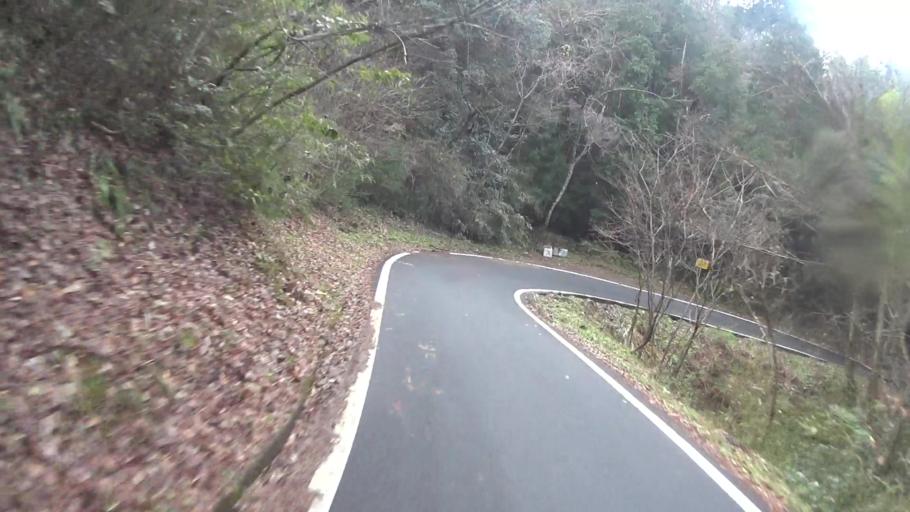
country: JP
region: Kyoto
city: Maizuru
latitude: 35.4394
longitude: 135.2979
